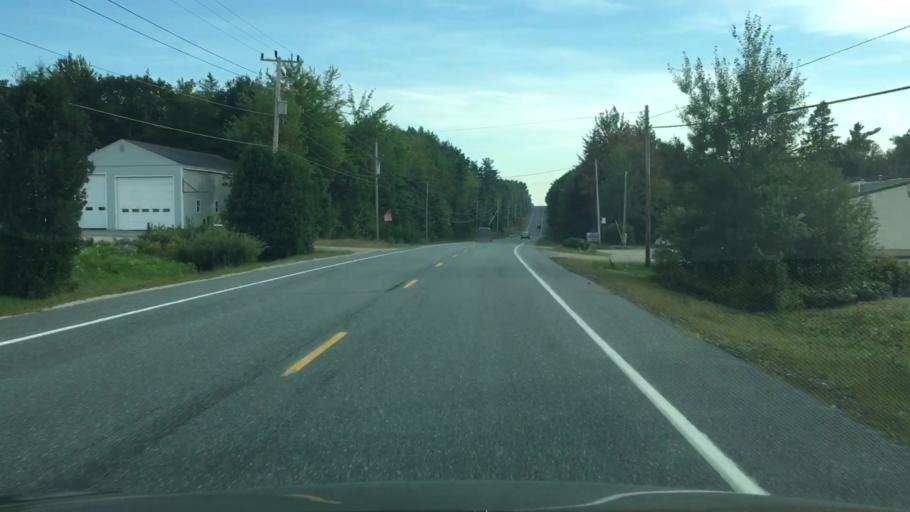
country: US
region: Maine
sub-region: Hancock County
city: Surry
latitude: 44.4853
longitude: -68.5137
